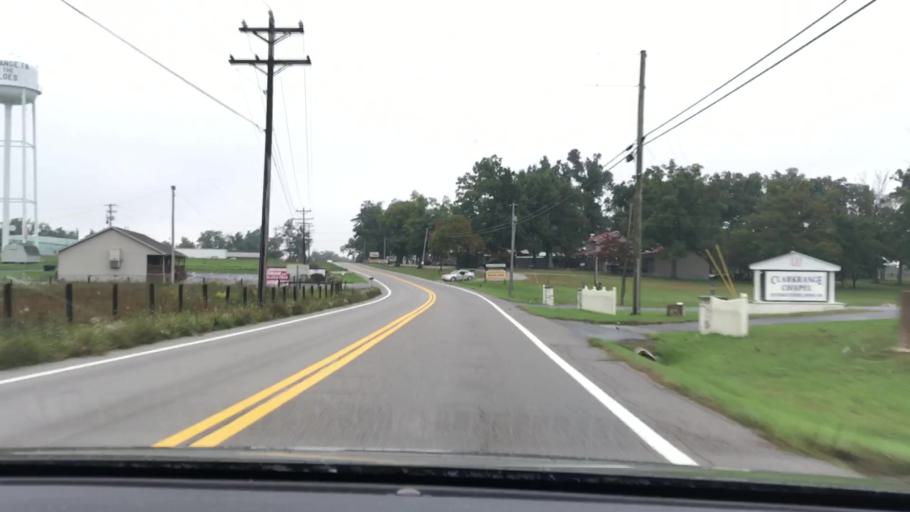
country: US
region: Tennessee
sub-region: Fentress County
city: Grimsley
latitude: 36.1908
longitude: -85.0202
